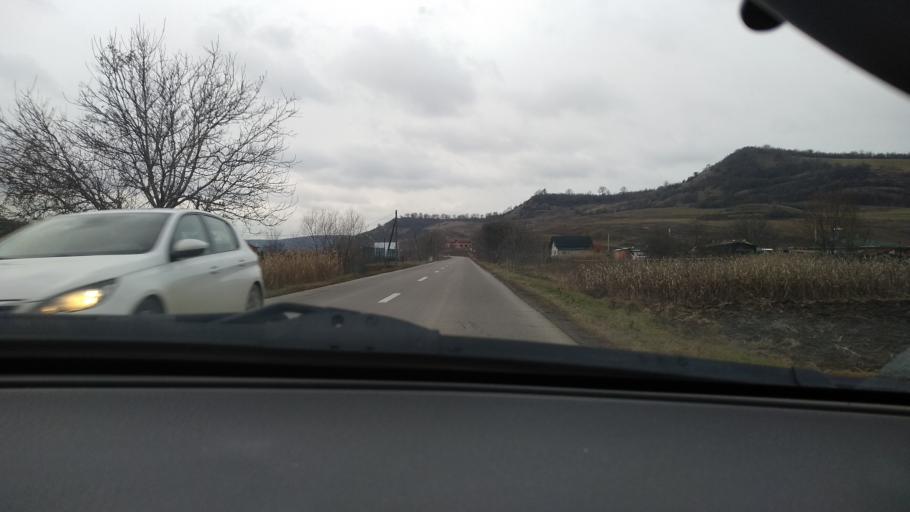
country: RO
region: Mures
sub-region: Comuna Livezeni
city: Livezeni
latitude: 46.5429
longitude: 24.6704
